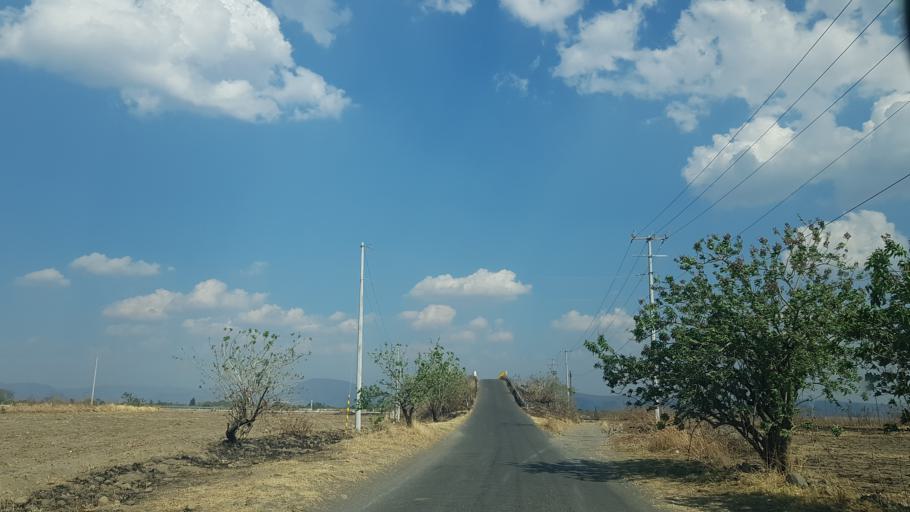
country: MX
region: Puebla
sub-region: Atlixco
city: Colonia Agricola de Ocotepec (Colonia San Jose)
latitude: 18.8879
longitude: -98.5002
